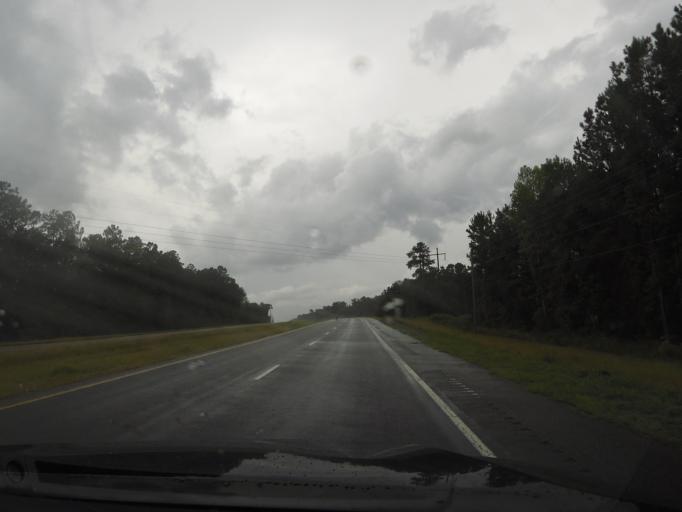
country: US
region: Georgia
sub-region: McIntosh County
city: Darien
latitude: 31.4245
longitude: -81.6688
